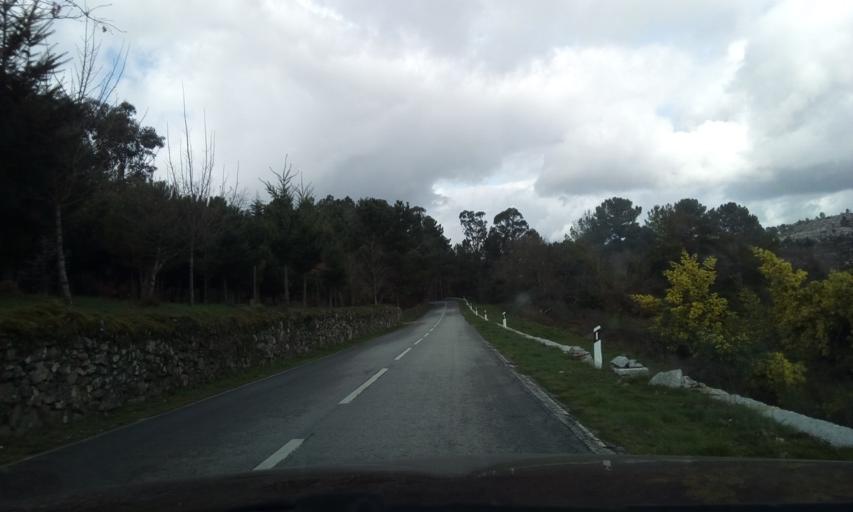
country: PT
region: Guarda
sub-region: Fornos de Algodres
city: Fornos de Algodres
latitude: 40.6562
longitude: -7.5545
